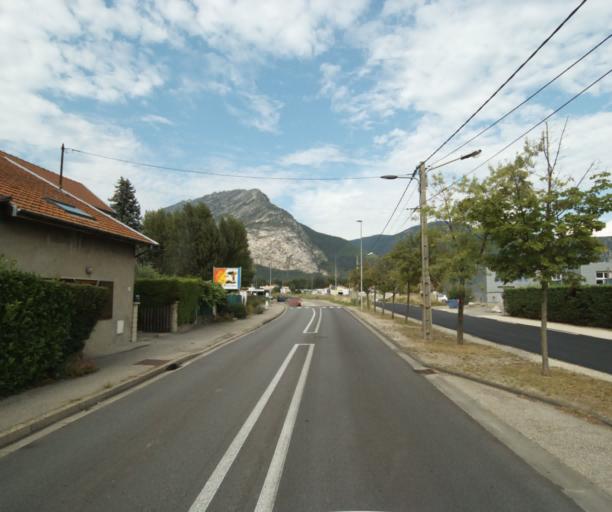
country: FR
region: Rhone-Alpes
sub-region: Departement de l'Isere
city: Fontaine
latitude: 45.2041
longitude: 5.6809
